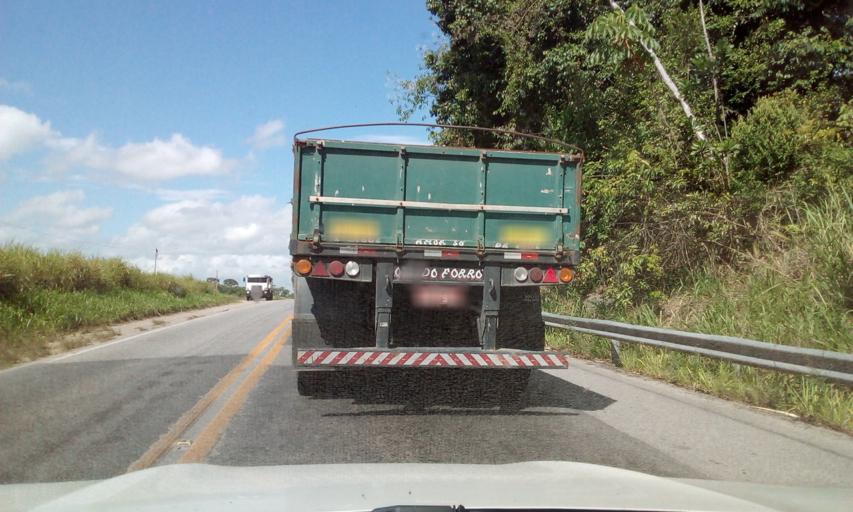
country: BR
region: Alagoas
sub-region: Pilar
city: Pilar
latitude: -9.5201
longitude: -35.9374
